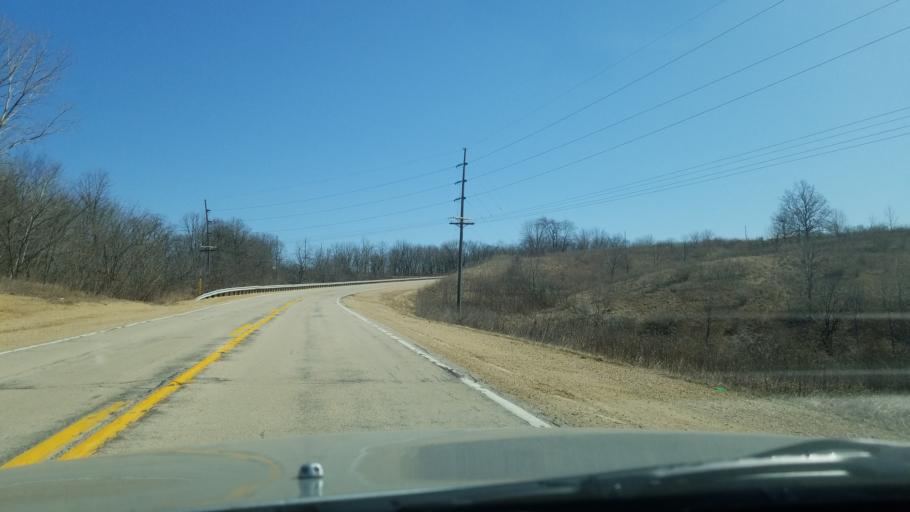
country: US
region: Wisconsin
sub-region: Iowa County
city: Mineral Point
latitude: 42.9033
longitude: -90.2287
